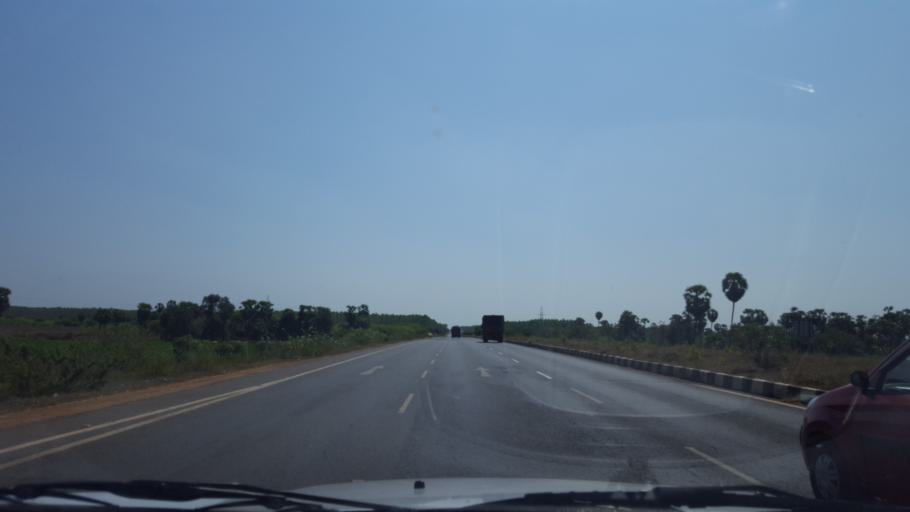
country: IN
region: Andhra Pradesh
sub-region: Nellore
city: Kovur
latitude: 14.6758
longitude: 79.9746
